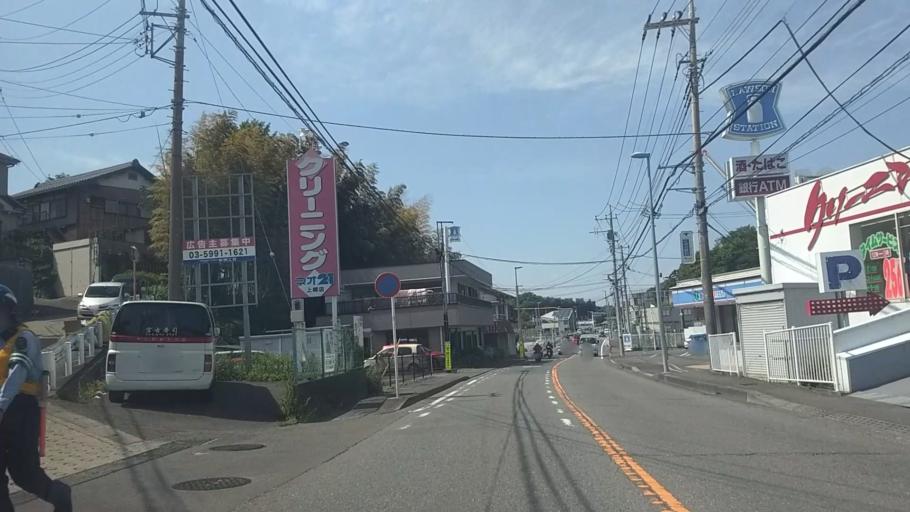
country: JP
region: Kanagawa
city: Kamakura
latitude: 35.3505
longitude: 139.5806
